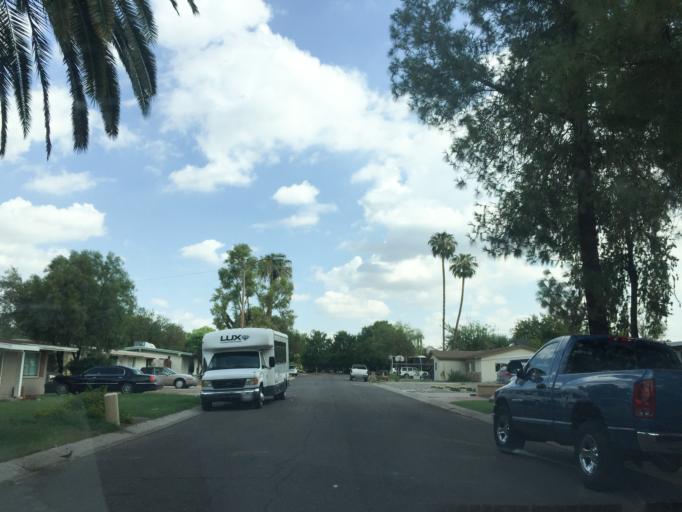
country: US
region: Arizona
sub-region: Maricopa County
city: Phoenix
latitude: 33.5316
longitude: -112.0535
